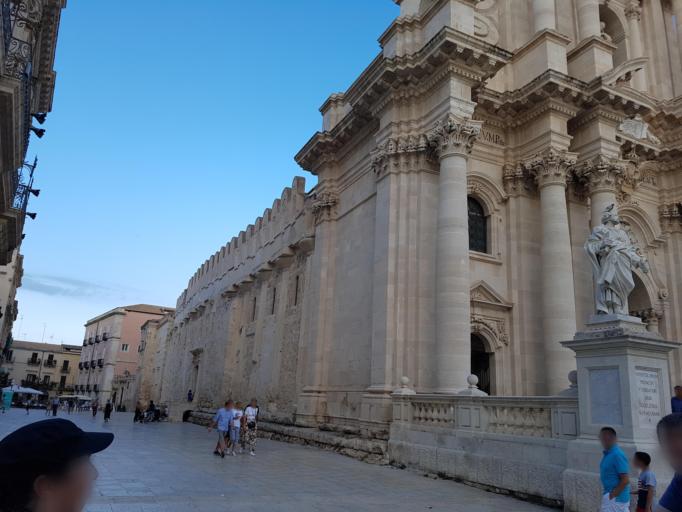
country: IT
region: Sicily
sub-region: Provincia di Siracusa
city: Siracusa
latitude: 37.0597
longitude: 15.2931
